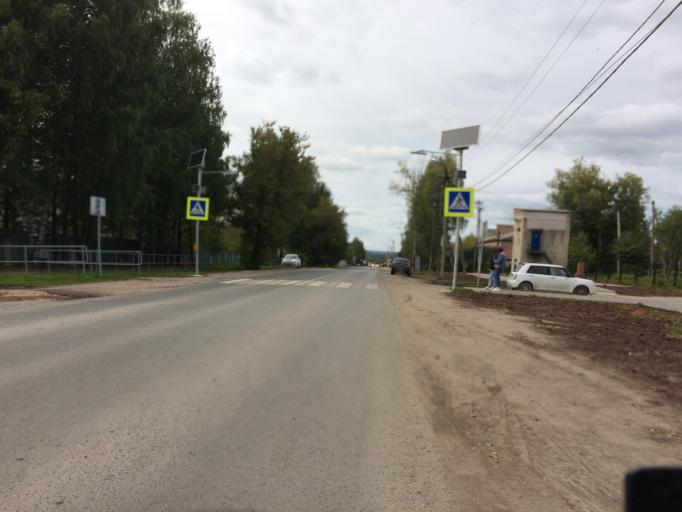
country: RU
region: Mariy-El
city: Yoshkar-Ola
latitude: 56.6547
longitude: 47.9767
